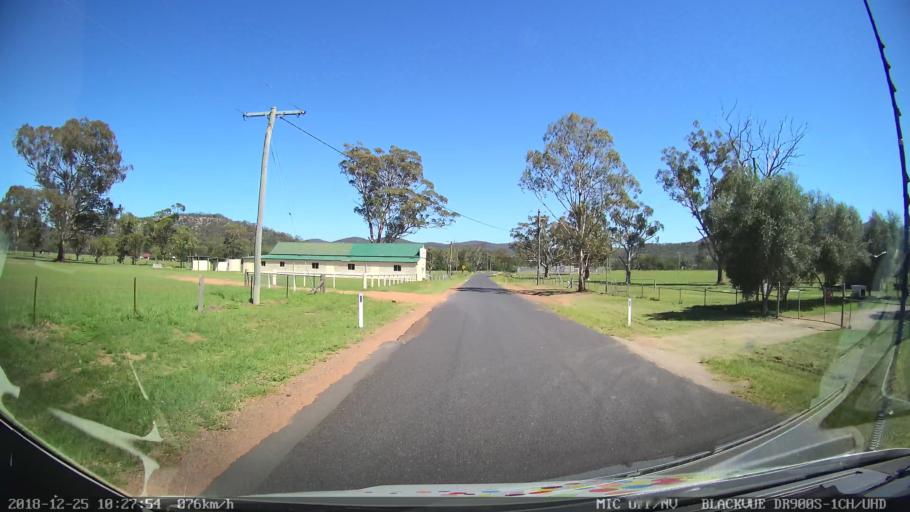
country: AU
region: New South Wales
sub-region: Muswellbrook
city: Denman
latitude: -32.3867
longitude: 150.4675
